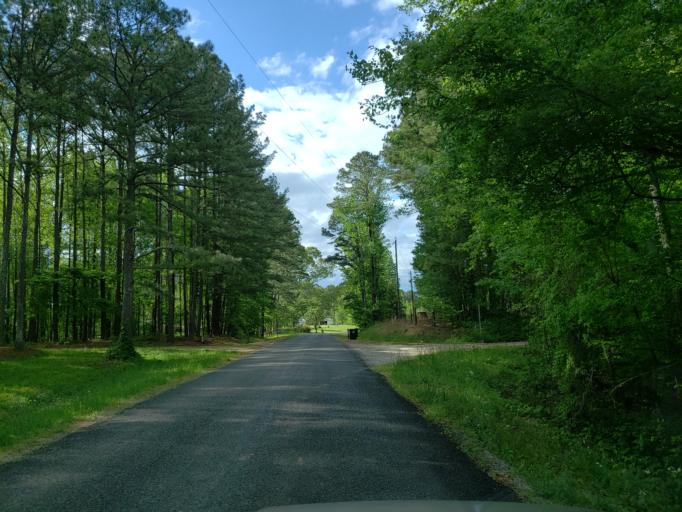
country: US
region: Georgia
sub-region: Haralson County
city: Tallapoosa
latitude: 33.7768
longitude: -85.3806
